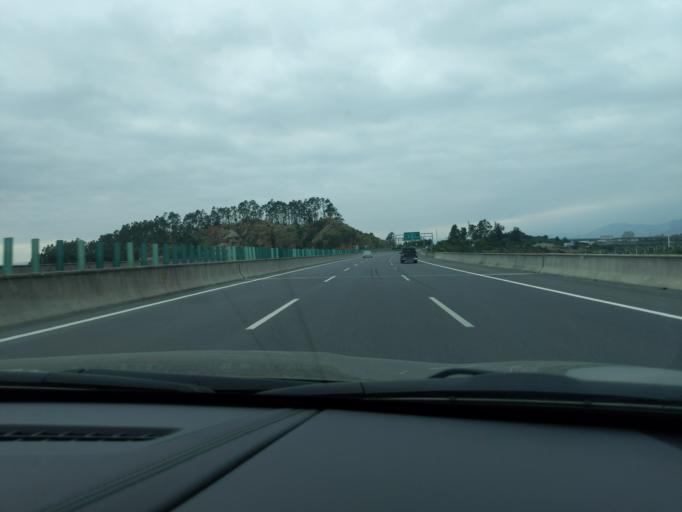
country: CN
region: Fujian
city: Neikeng
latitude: 24.7838
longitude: 118.4876
